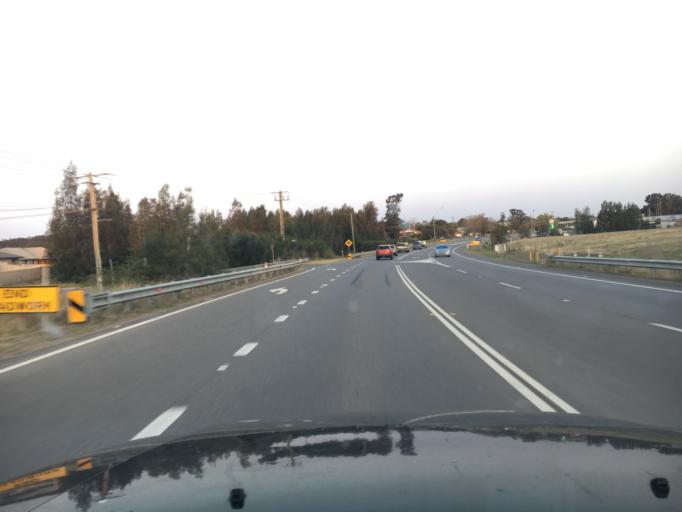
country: AU
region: New South Wales
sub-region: Cessnock
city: Greta
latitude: -32.6736
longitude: 151.3845
